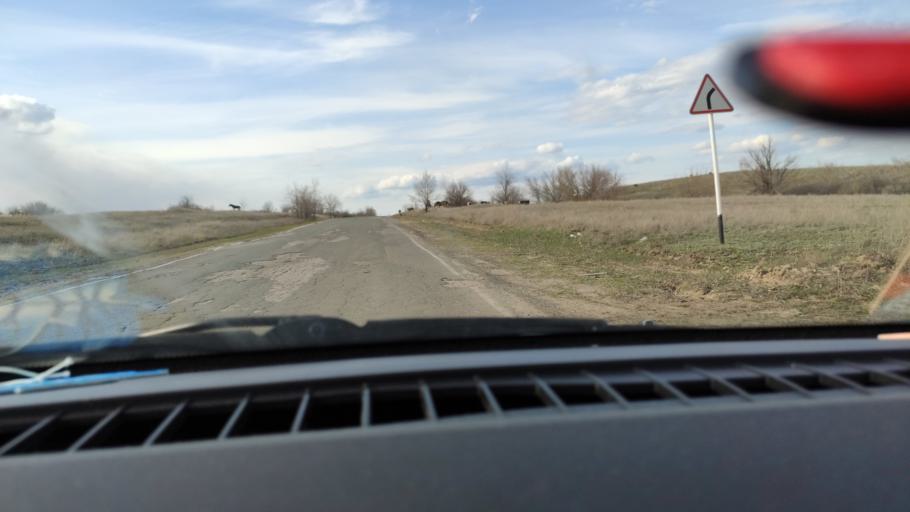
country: RU
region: Saratov
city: Rovnoye
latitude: 50.9650
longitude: 46.1169
